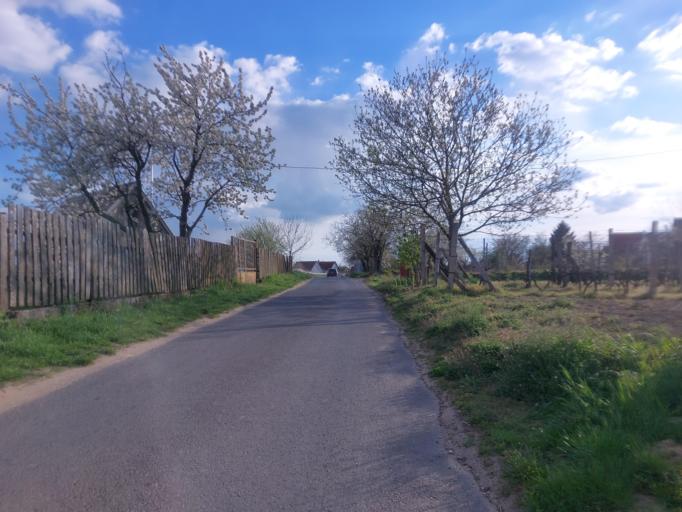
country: HU
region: Veszprem
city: Devecser
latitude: 47.1387
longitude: 17.3852
